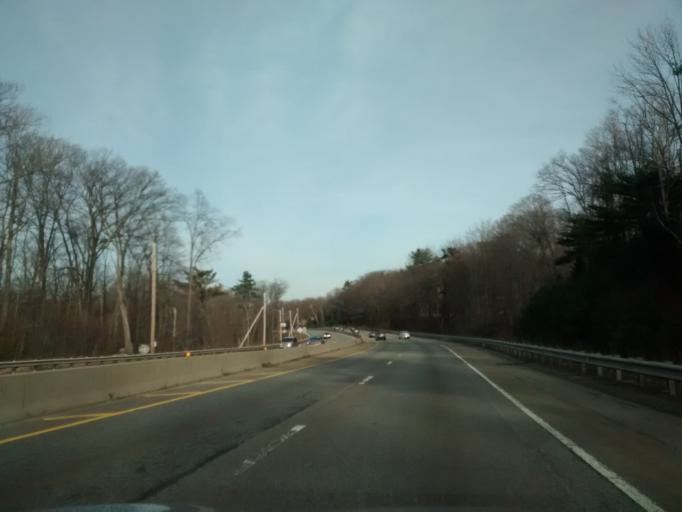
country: US
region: Massachusetts
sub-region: Worcester County
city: Charlton
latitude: 42.1469
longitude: -71.9388
